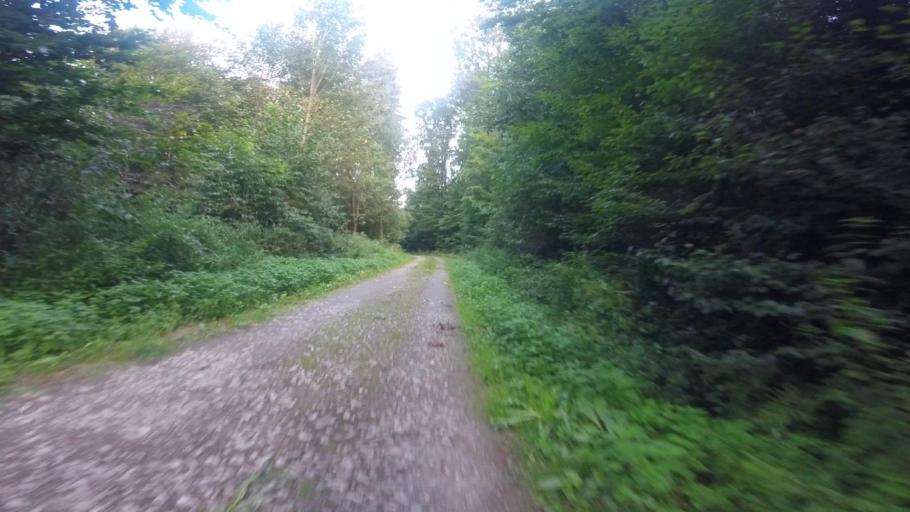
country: DE
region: Baden-Wuerttemberg
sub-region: Regierungsbezirk Stuttgart
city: Aspach
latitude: 48.9726
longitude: 9.3646
